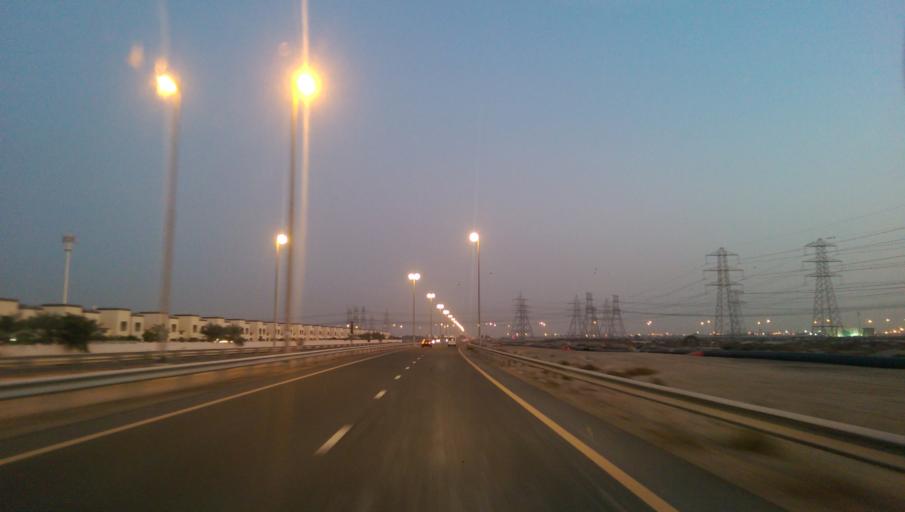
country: AE
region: Dubai
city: Dubai
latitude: 25.0369
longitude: 55.1606
